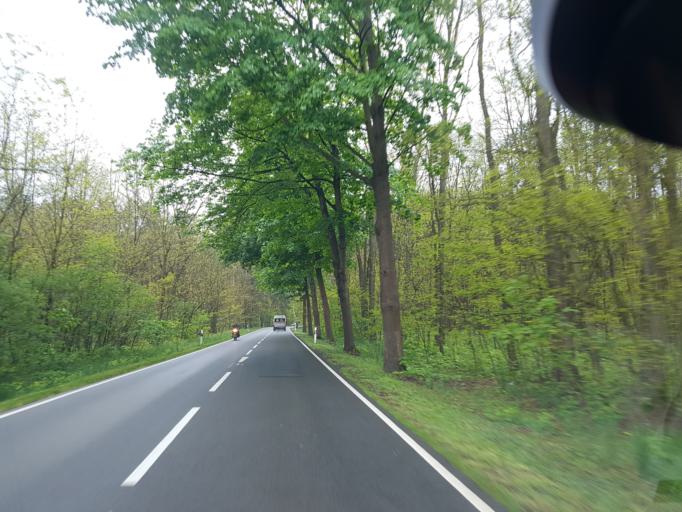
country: DE
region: Saxony
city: Schleife
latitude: 51.6108
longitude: 14.4838
